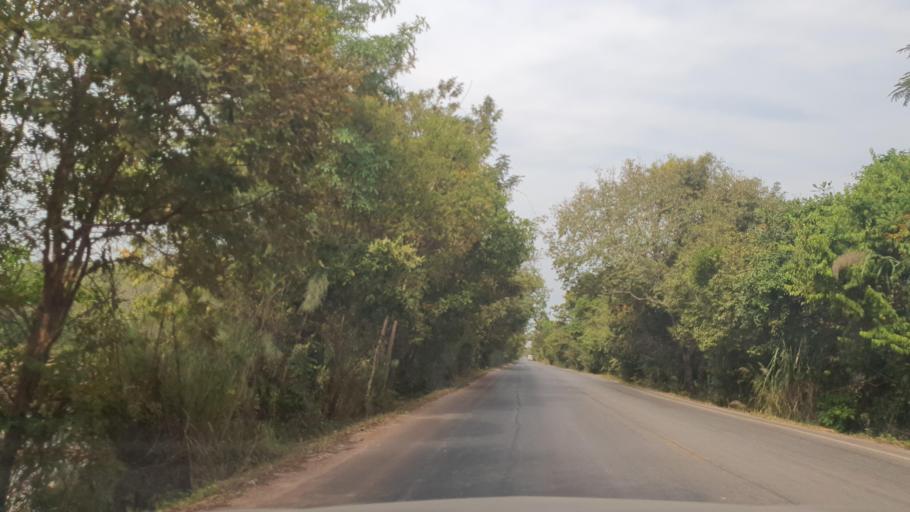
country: TH
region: Changwat Bueng Kan
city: Bung Khla
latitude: 18.2157
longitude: 104.0415
